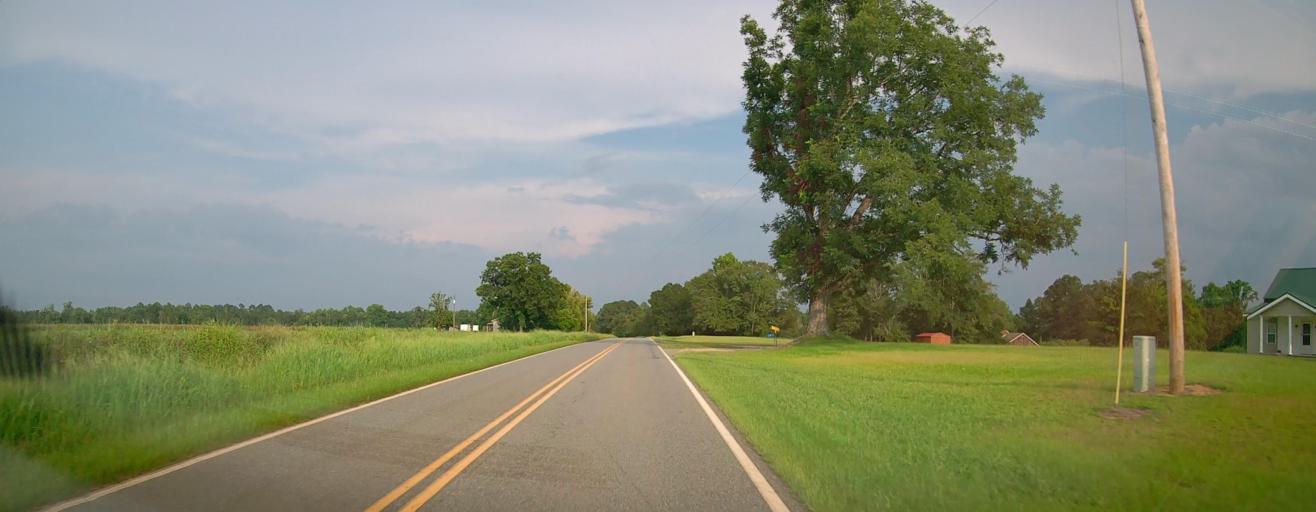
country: US
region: Georgia
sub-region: Laurens County
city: Dublin
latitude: 32.4822
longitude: -82.9668
